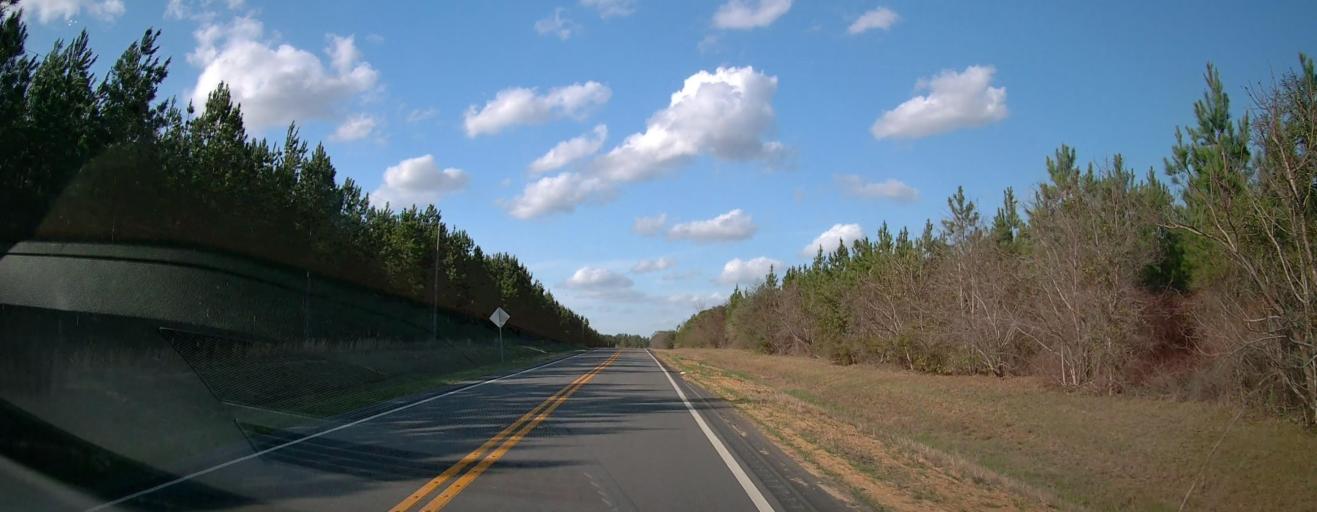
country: US
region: Georgia
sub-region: Wheeler County
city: Alamo
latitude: 32.0814
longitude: -82.8113
